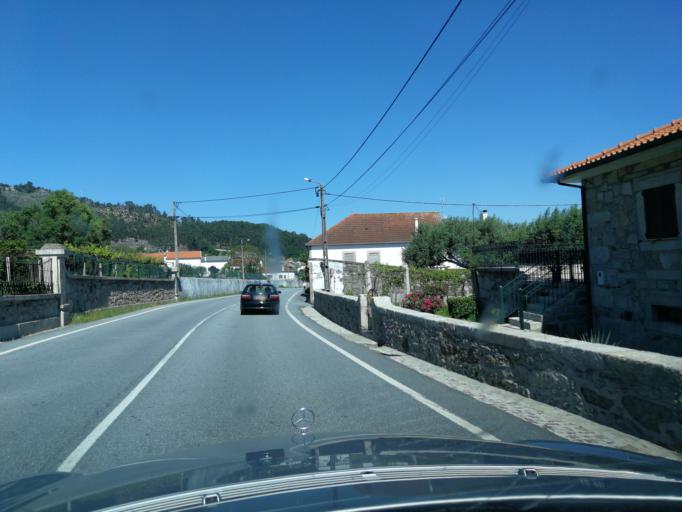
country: PT
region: Viana do Castelo
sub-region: Viana do Castelo
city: Darque
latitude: 41.7115
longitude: -8.7599
